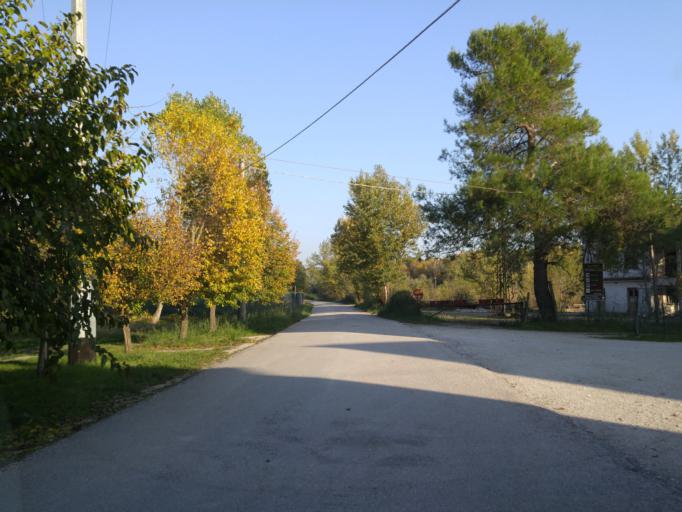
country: IT
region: The Marches
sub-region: Provincia di Pesaro e Urbino
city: Montefelcino
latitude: 43.7122
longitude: 12.8530
